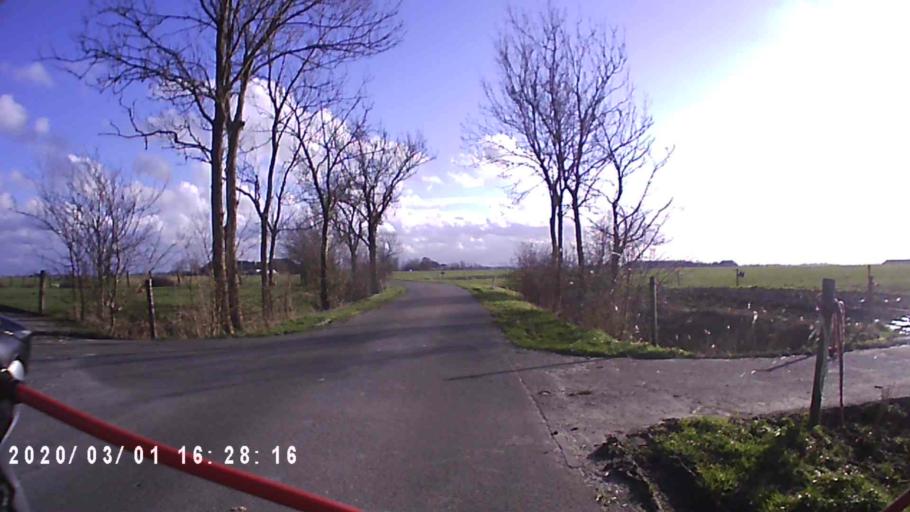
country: NL
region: Groningen
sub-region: Gemeente Zuidhorn
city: Oldehove
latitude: 53.3036
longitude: 6.4287
